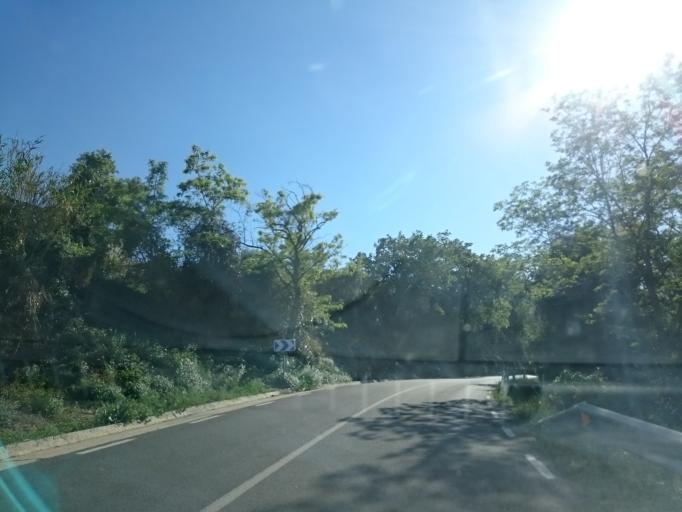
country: ES
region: Catalonia
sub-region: Provincia de Barcelona
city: Sant Boi de Llobregat
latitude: 41.3445
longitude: 2.0139
